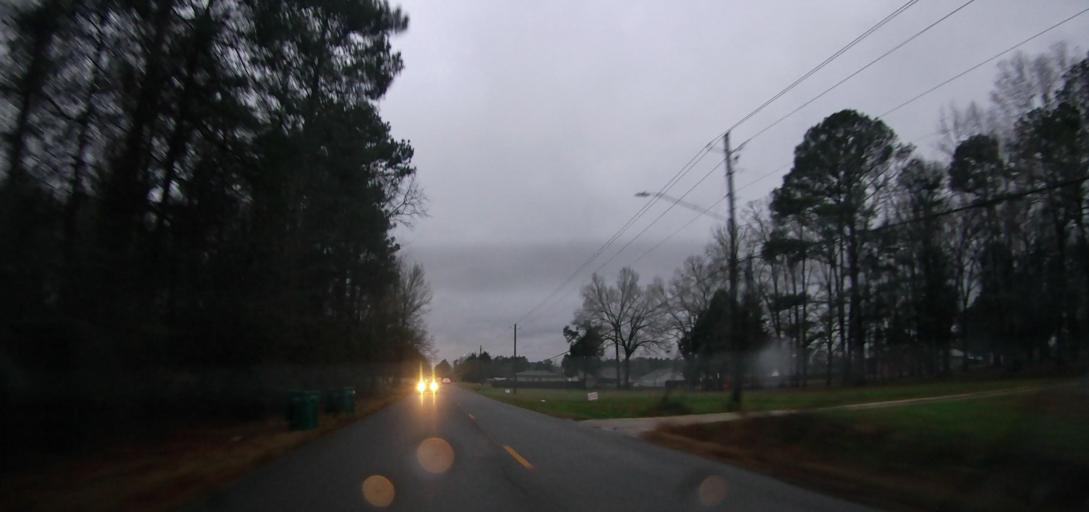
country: US
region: Alabama
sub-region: Tuscaloosa County
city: Vance
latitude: 33.1475
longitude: -87.2298
